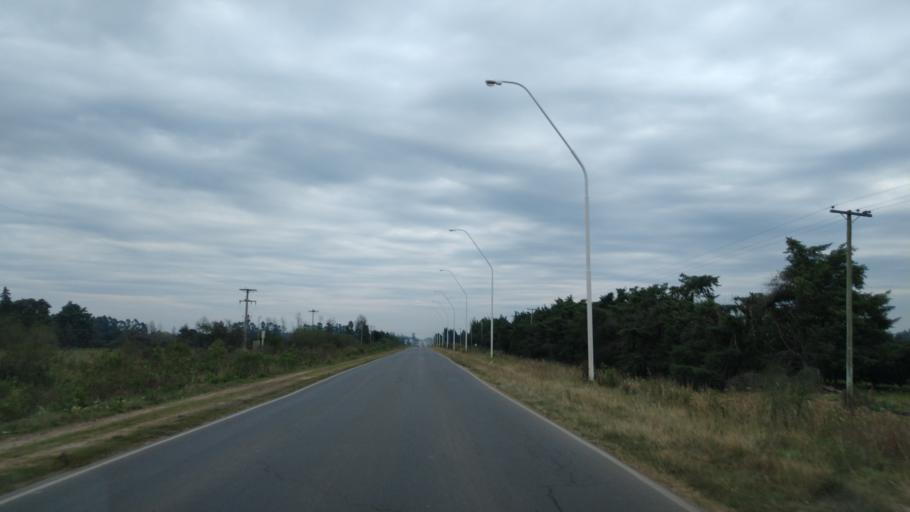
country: AR
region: Entre Rios
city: Villa del Rosario
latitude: -30.7870
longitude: -57.9473
